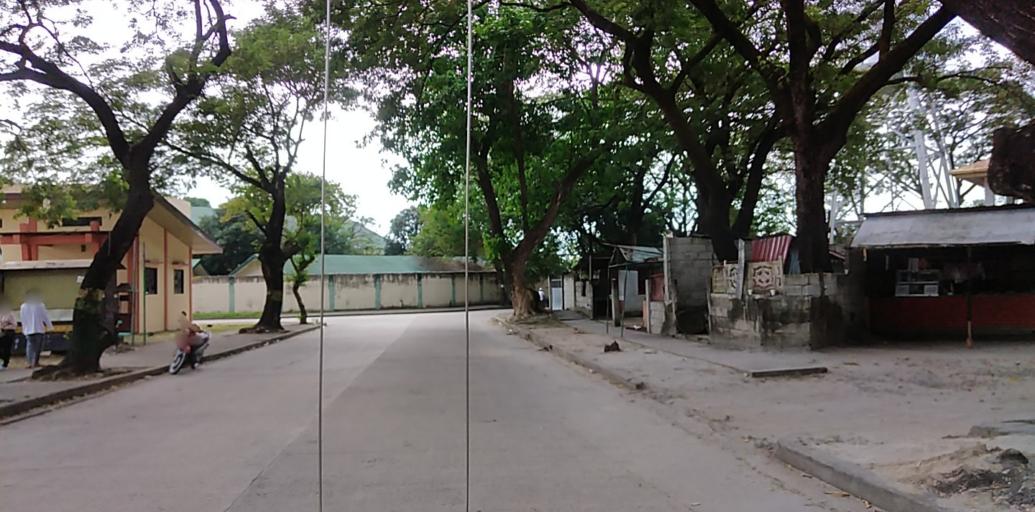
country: PH
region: Central Luzon
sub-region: Province of Pampanga
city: Pio
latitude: 15.0443
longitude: 120.5288
